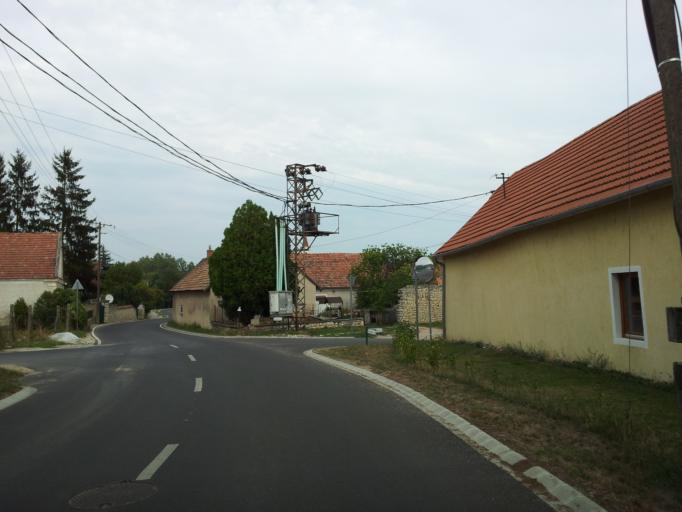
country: HU
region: Veszprem
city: Balatonfured
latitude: 46.9542
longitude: 17.7810
